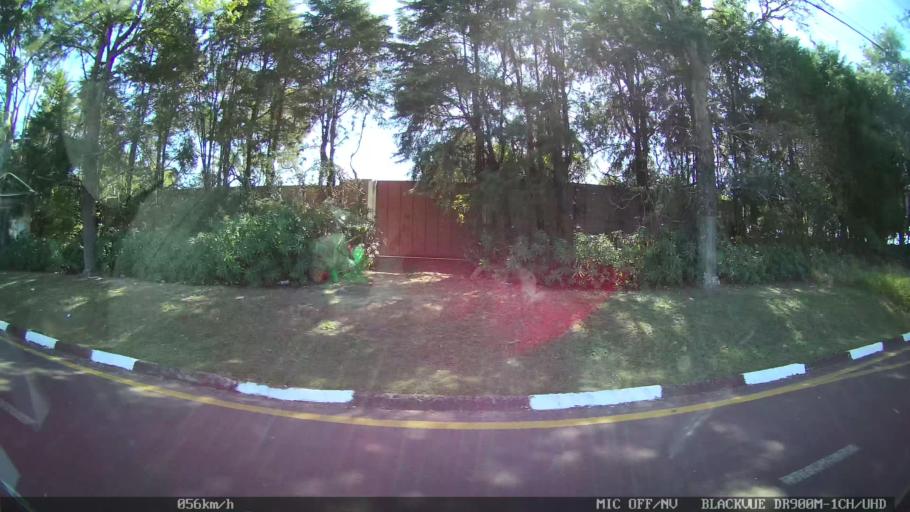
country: BR
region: Sao Paulo
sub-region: Franca
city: Franca
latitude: -20.5642
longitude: -47.3612
